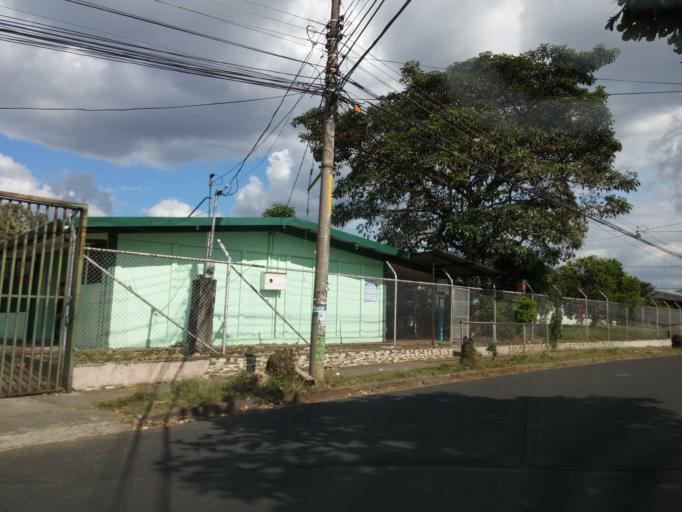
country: CR
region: Alajuela
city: Alajuela
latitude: 10.0092
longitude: -84.2040
